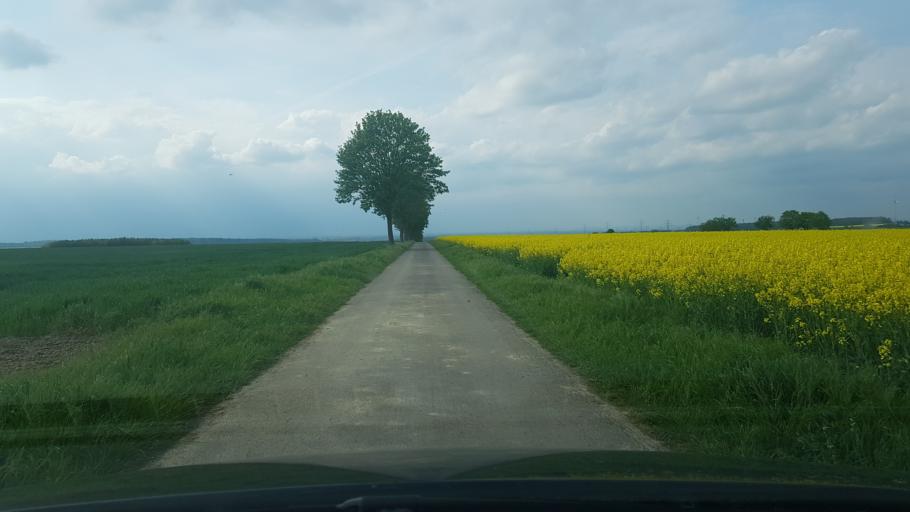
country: DE
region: North Rhine-Westphalia
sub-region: Regierungsbezirk Detmold
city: Paderborn
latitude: 51.6496
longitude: 8.7533
